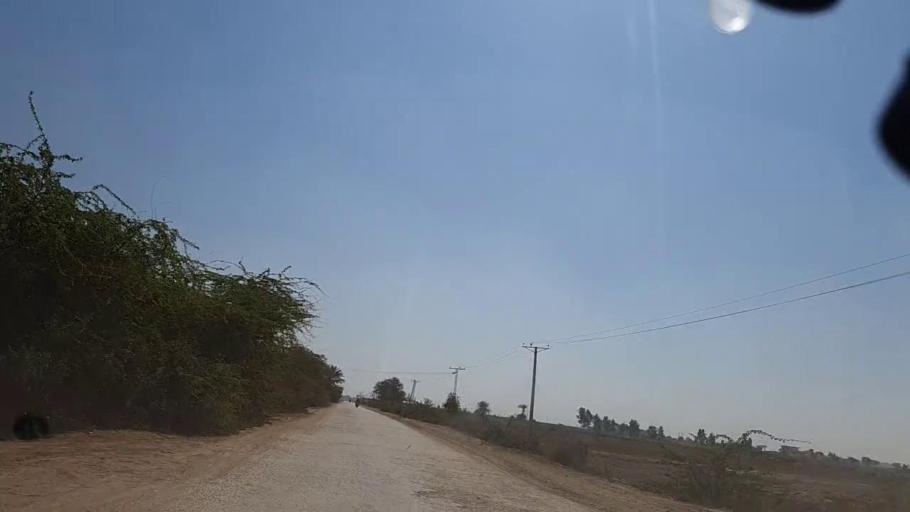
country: PK
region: Sindh
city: Mirpur Khas
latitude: 25.4992
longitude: 69.0354
